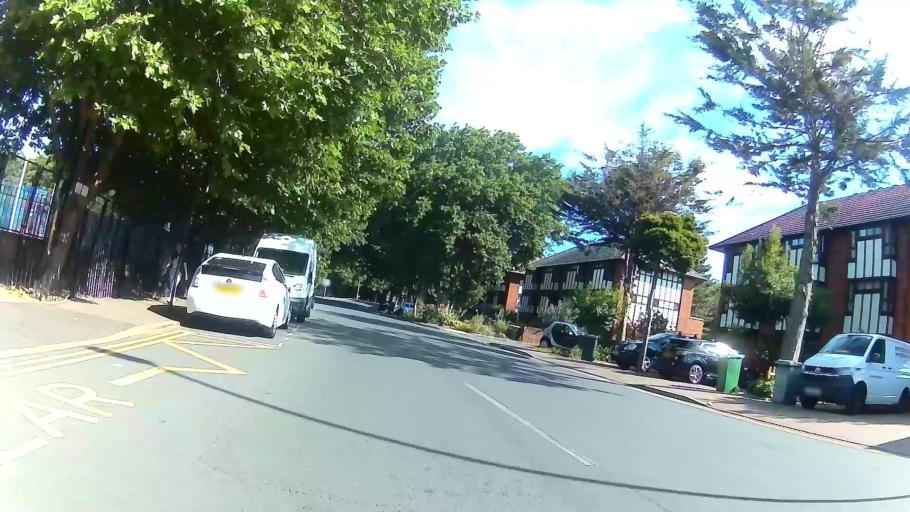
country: GB
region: England
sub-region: Greater London
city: Woolwich
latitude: 51.5111
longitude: 0.0622
